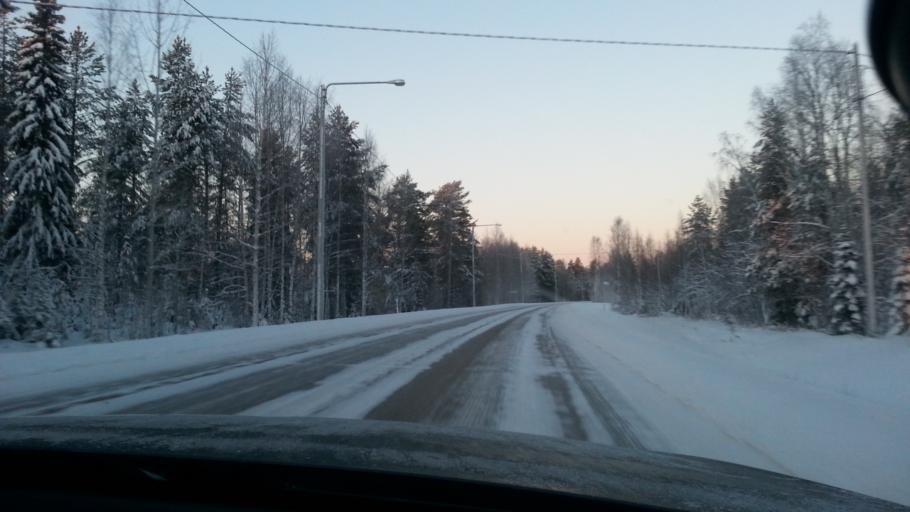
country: FI
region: Lapland
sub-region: Tunturi-Lappi
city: Kittilae
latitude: 67.0423
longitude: 25.0969
